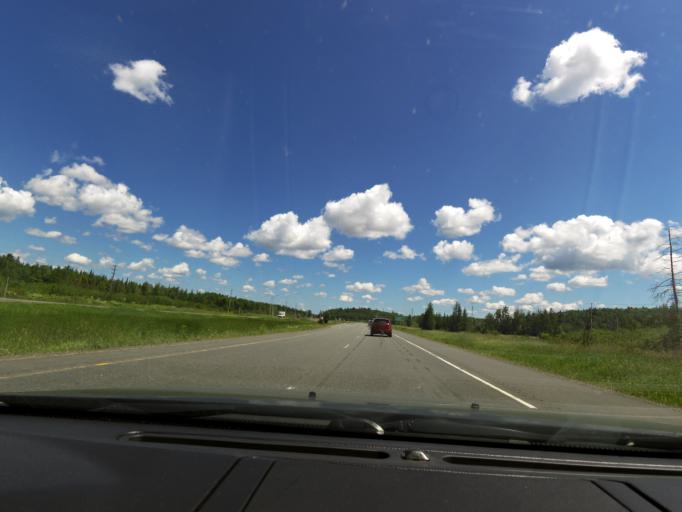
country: CA
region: Ontario
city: Huntsville
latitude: 45.2350
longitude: -79.3028
